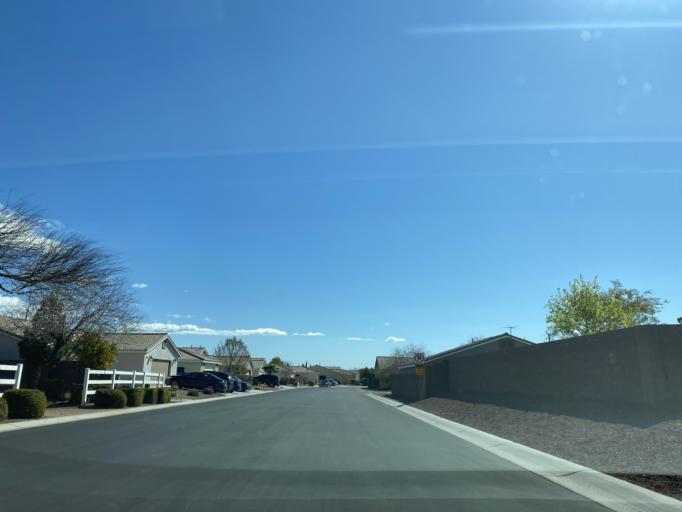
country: US
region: Nevada
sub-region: Clark County
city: North Las Vegas
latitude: 36.3301
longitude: -115.2688
